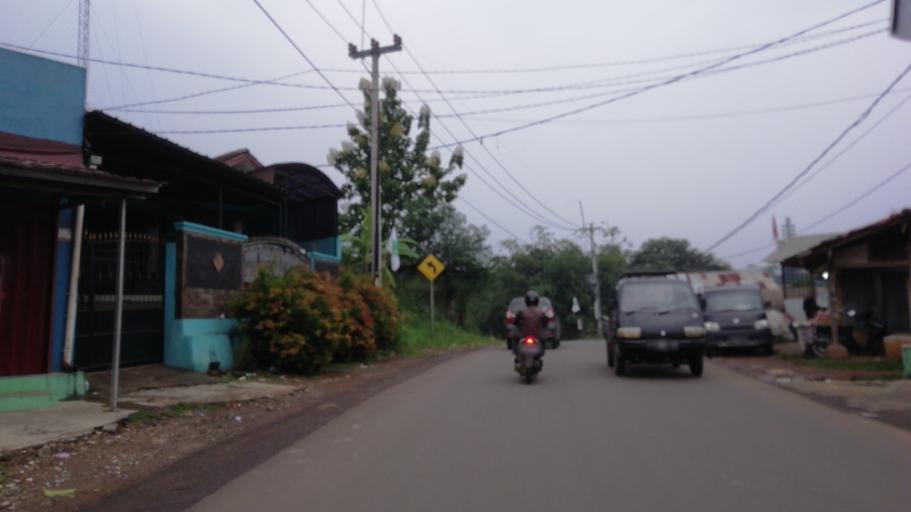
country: ID
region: West Java
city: Bogor
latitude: -6.5304
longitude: 106.8052
